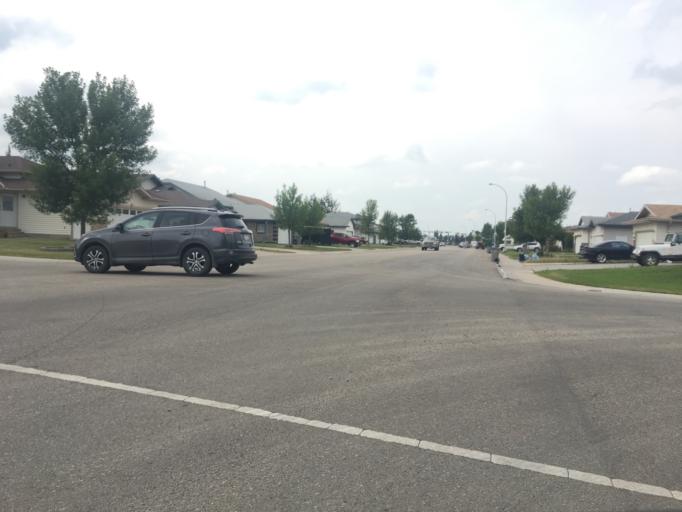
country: CA
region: Alberta
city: Grande Prairie
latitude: 55.1490
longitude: -118.8156
